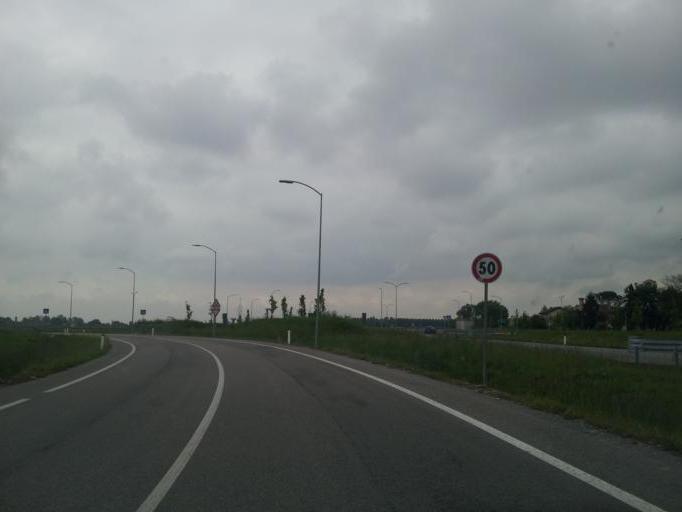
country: IT
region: Friuli Venezia Giulia
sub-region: Provincia di Udine
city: Varmo
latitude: 45.9064
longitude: 13.0031
